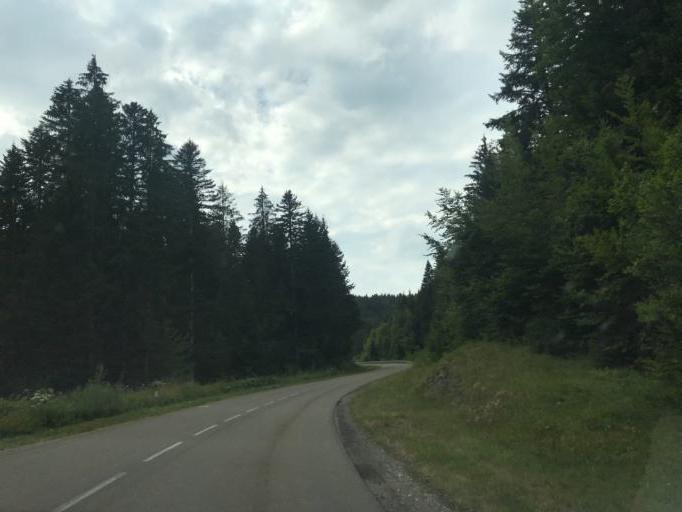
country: FR
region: Franche-Comte
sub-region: Departement du Jura
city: Longchaumois
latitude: 46.5004
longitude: 5.9122
